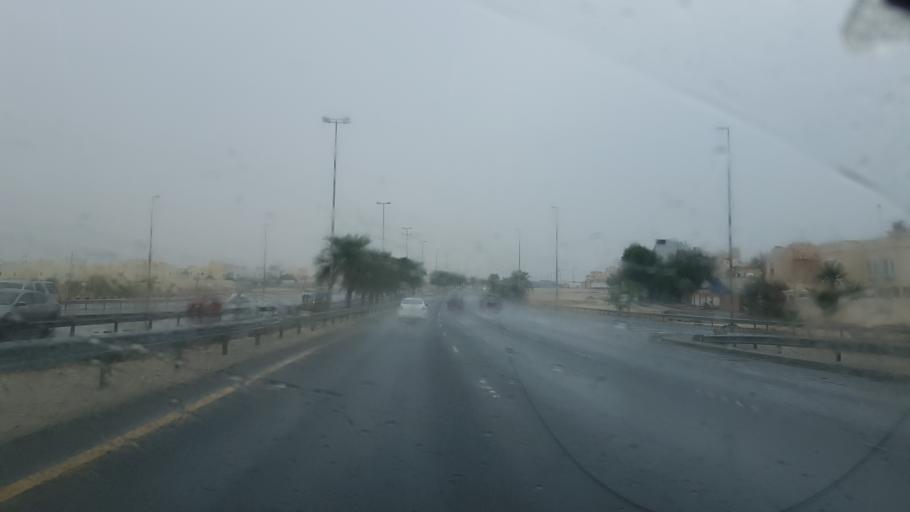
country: BH
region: Central Governorate
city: Madinat Hamad
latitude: 26.1369
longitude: 50.5103
